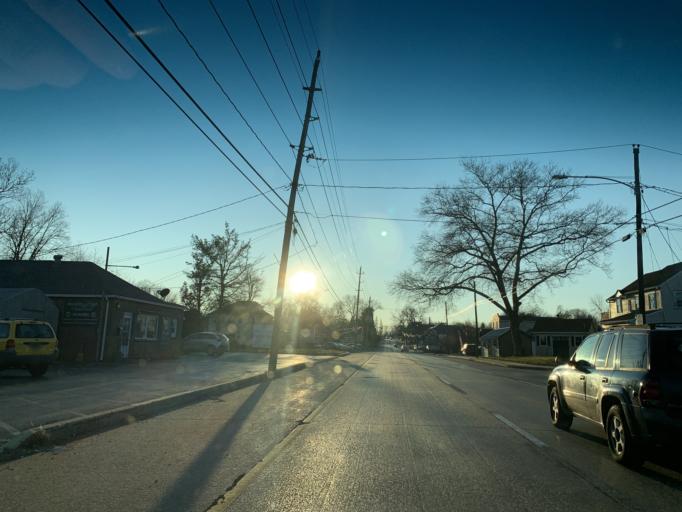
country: US
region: Delaware
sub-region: New Castle County
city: Newport
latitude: 39.7149
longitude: -75.6426
